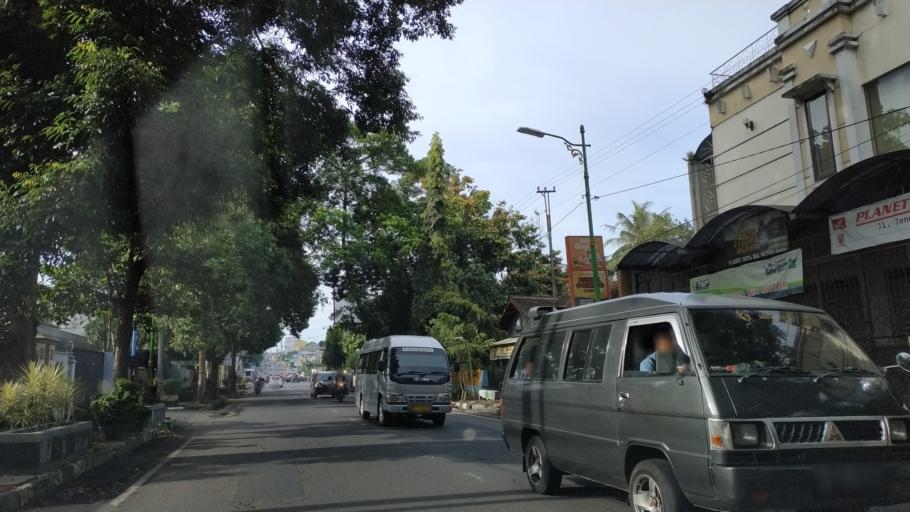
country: ID
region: Central Java
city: Salatiga
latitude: -7.3415
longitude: 110.5095
